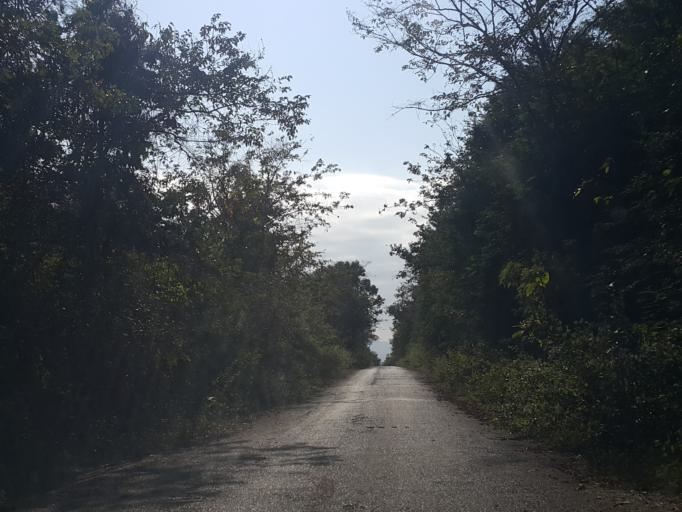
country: TH
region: Lampang
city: Mae Mo
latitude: 18.3040
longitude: 99.6625
